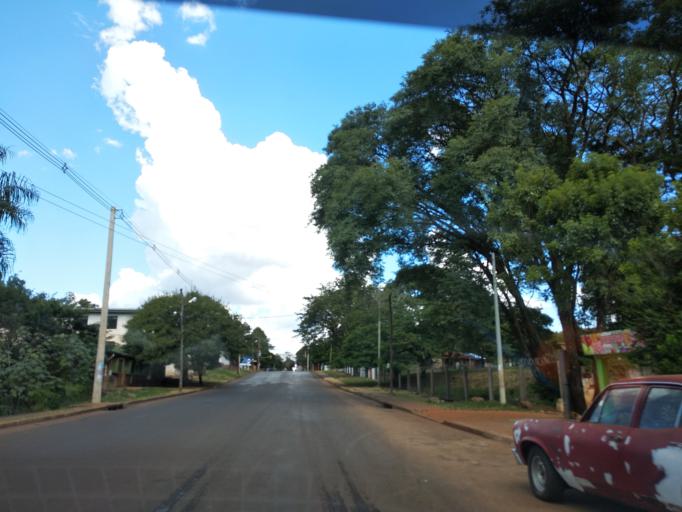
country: AR
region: Misiones
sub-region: Departamento de Capital
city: Posadas
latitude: -27.3574
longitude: -55.9152
